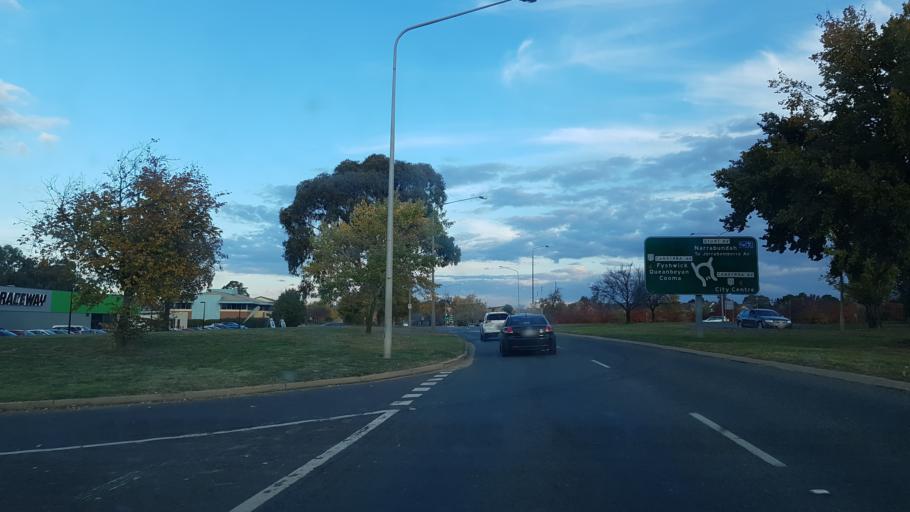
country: AU
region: Australian Capital Territory
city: Forrest
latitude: -35.3214
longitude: 149.1487
